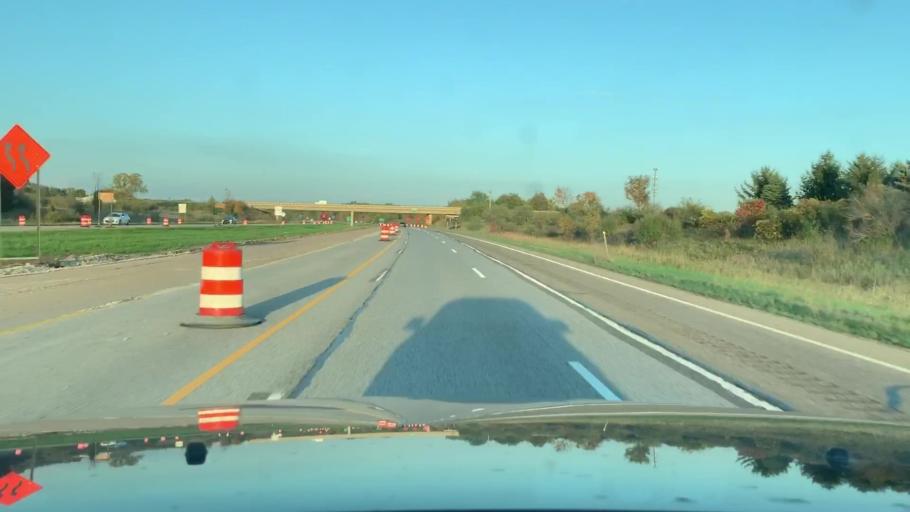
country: US
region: Michigan
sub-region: Ottawa County
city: Jenison
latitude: 42.8650
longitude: -85.8051
